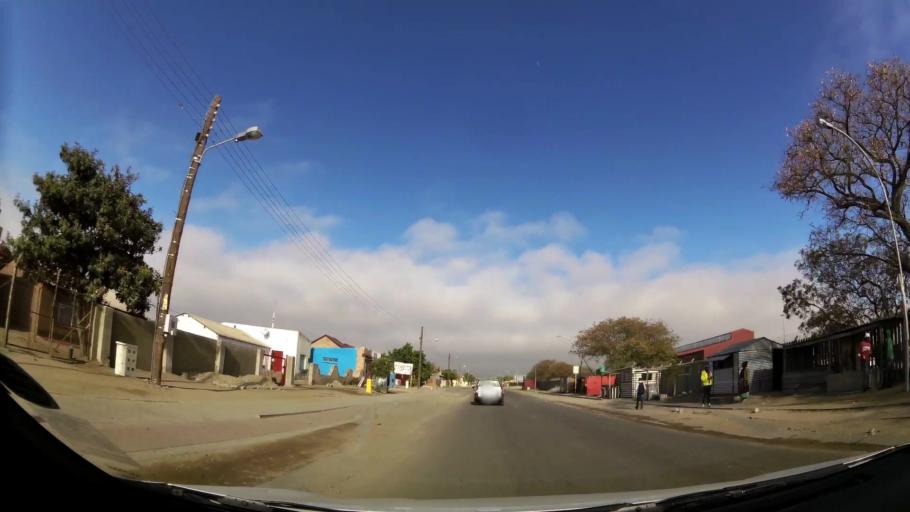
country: ZA
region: Limpopo
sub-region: Capricorn District Municipality
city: Polokwane
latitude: -23.8431
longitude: 29.3915
